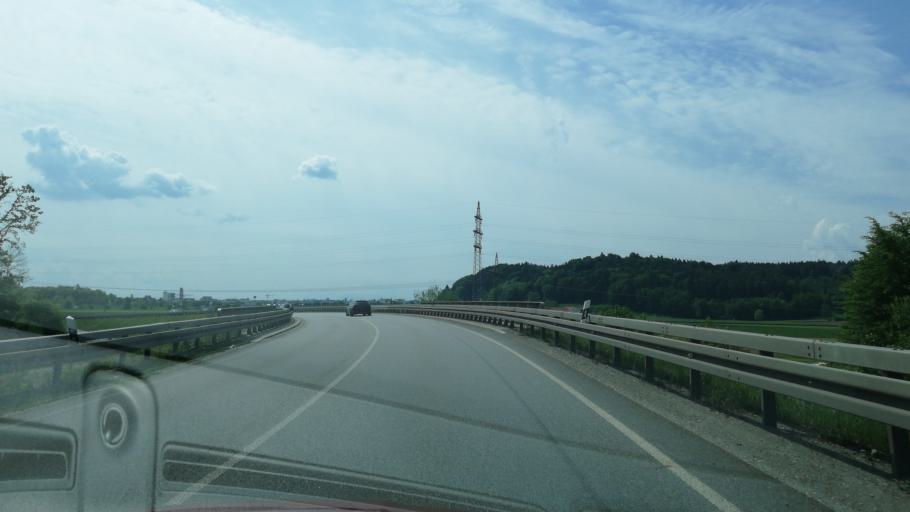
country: DE
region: Bavaria
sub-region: Upper Bavaria
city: Burghausen
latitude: 48.1860
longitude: 12.8204
